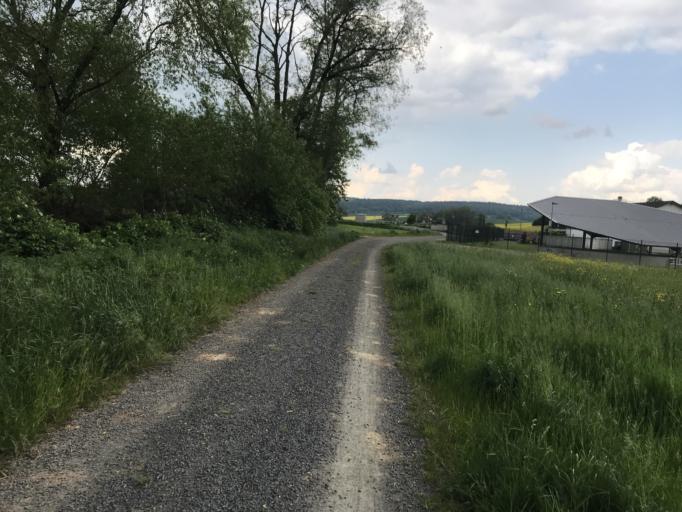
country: DE
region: Hesse
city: Budingen
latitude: 50.2896
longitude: 9.0830
